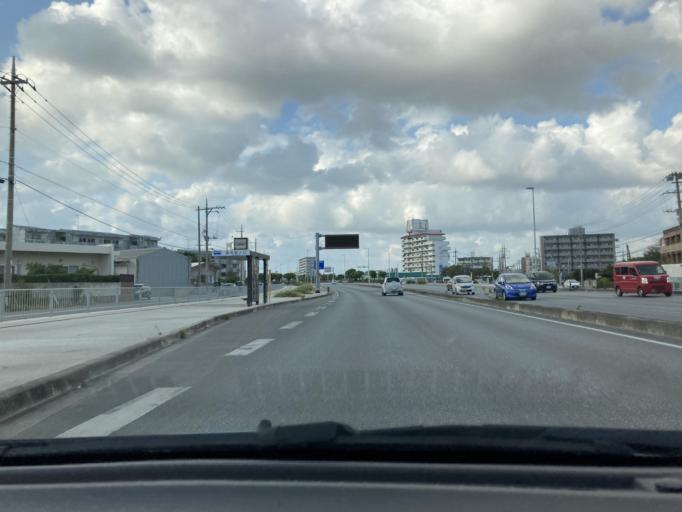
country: JP
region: Okinawa
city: Itoman
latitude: 26.1171
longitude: 127.6685
